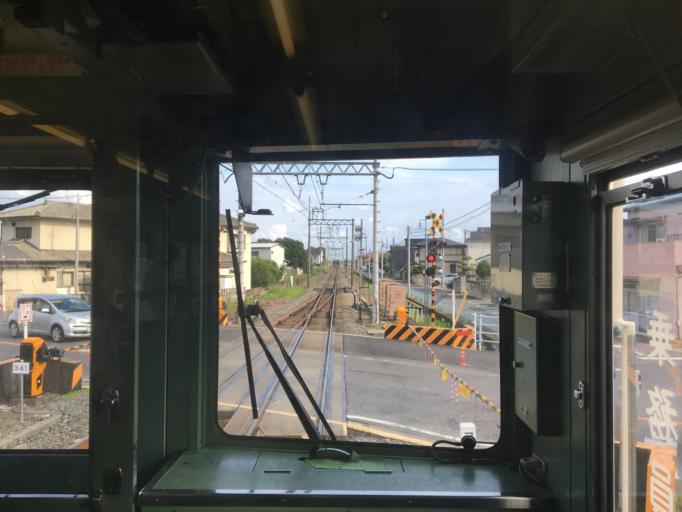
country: JP
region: Tochigi
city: Ashikaga
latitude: 36.3040
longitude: 139.4591
